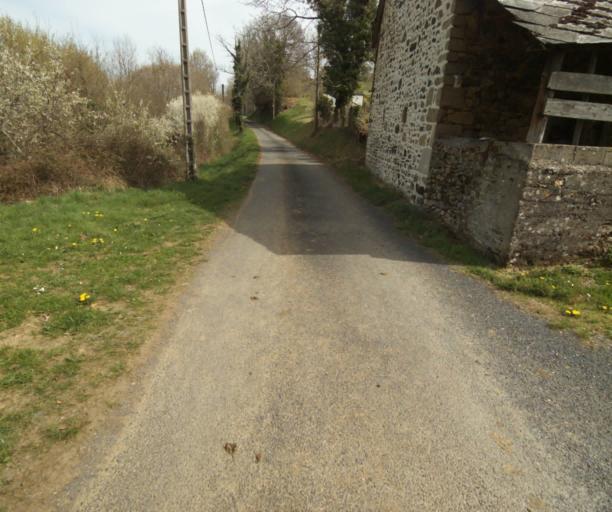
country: FR
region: Limousin
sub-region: Departement de la Correze
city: Naves
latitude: 45.3276
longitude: 1.7995
